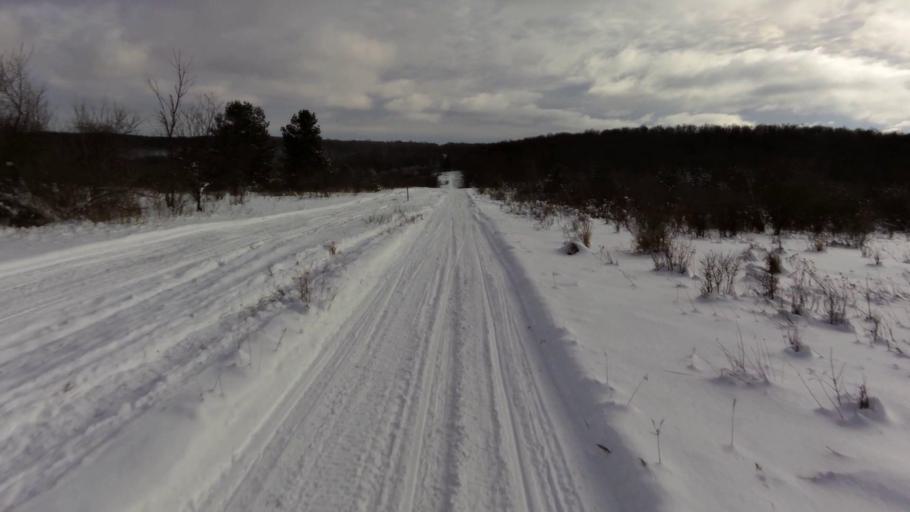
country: US
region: New York
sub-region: Cattaraugus County
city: Franklinville
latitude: 42.3142
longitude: -78.5368
